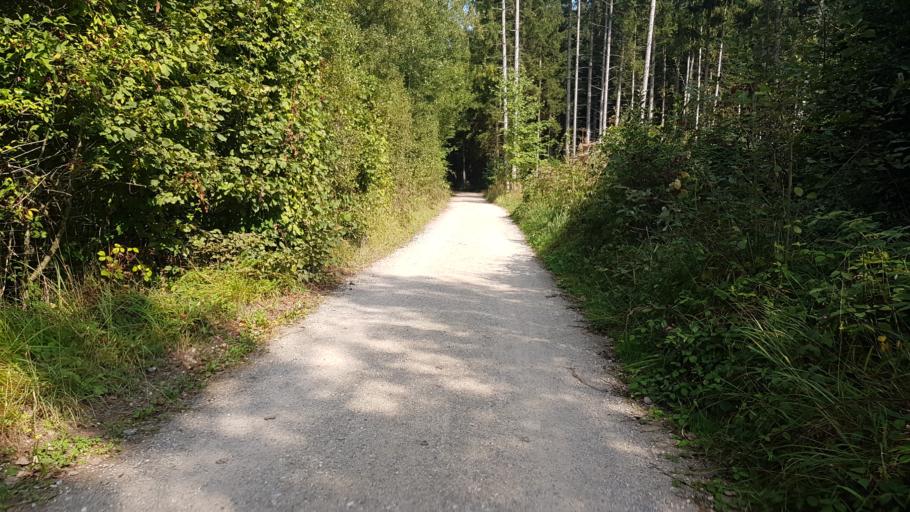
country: DE
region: Bavaria
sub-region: Upper Bavaria
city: Gilching
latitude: 48.0879
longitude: 11.3033
